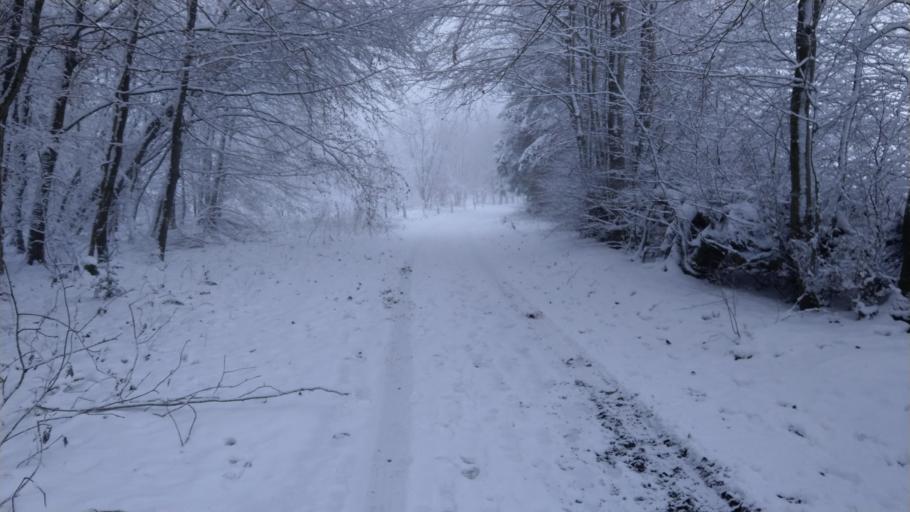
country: DE
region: North Rhine-Westphalia
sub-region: Regierungsbezirk Koln
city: Monschau
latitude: 50.5704
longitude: 6.2050
